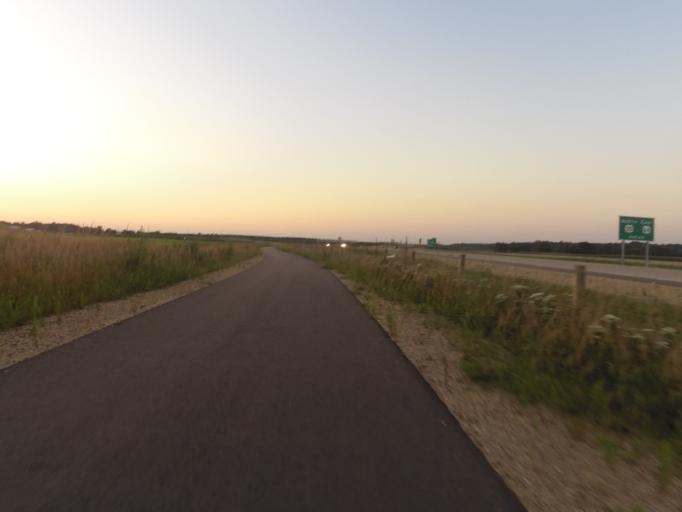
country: US
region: Minnesota
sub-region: Washington County
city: Oak Park Heights
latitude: 45.0530
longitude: -92.7795
